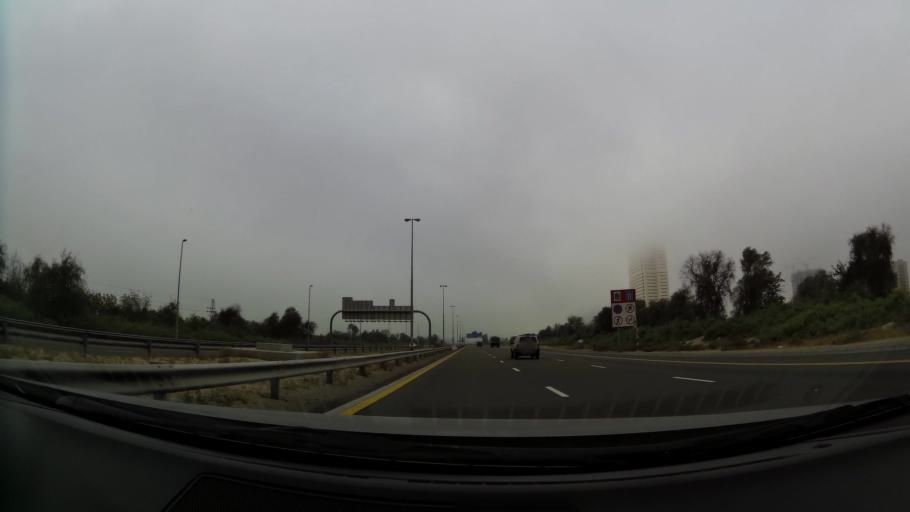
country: AE
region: Dubai
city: Dubai
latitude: 25.0998
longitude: 55.3816
